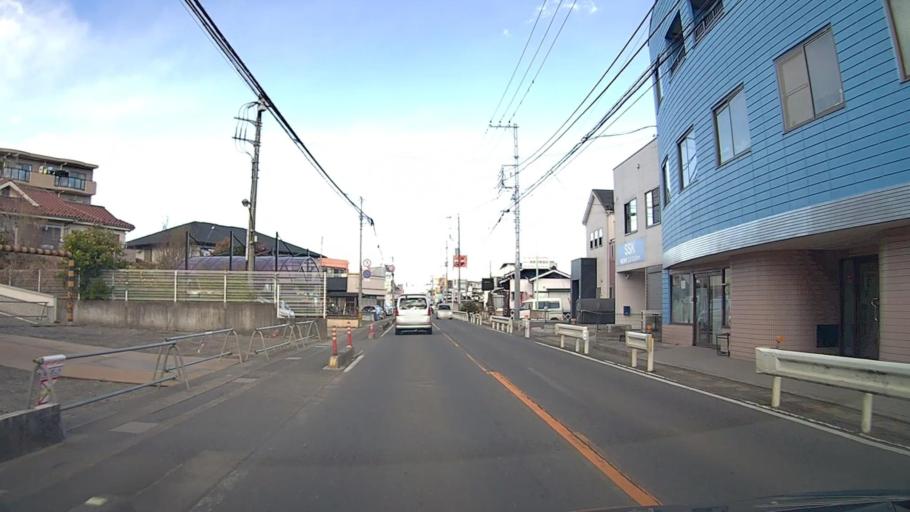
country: JP
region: Saitama
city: Asaka
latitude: 35.7792
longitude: 139.5713
